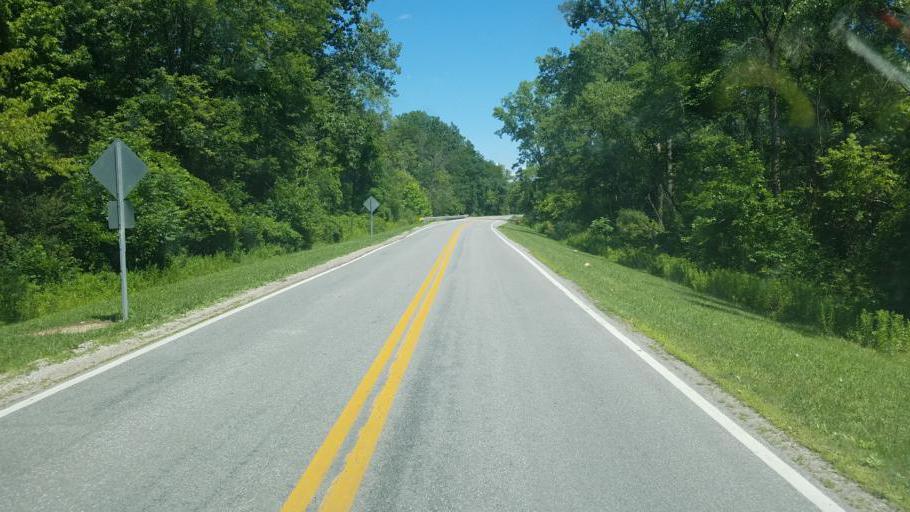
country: US
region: Ohio
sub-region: Delaware County
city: Sunbury
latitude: 40.2365
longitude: -82.8964
